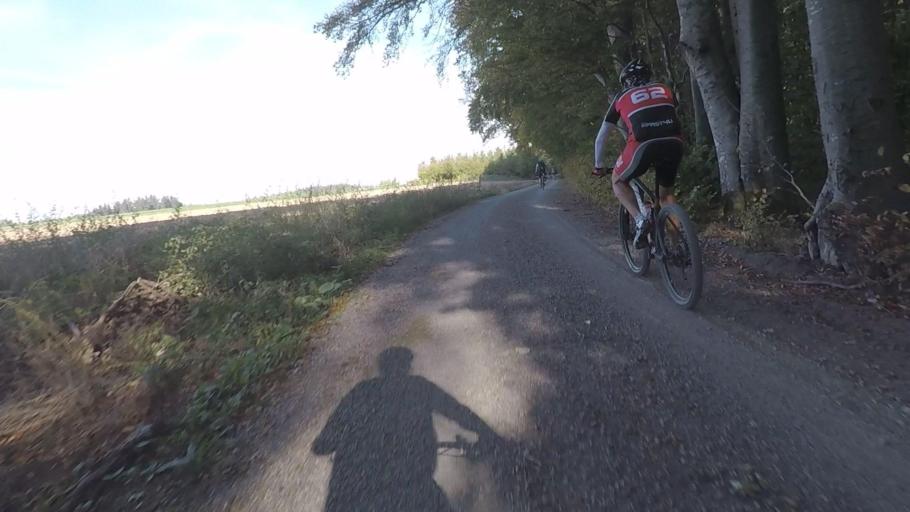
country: DE
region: Baden-Wuerttemberg
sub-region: Regierungsbezirk Stuttgart
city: Wustenrot
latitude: 49.0635
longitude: 9.4802
